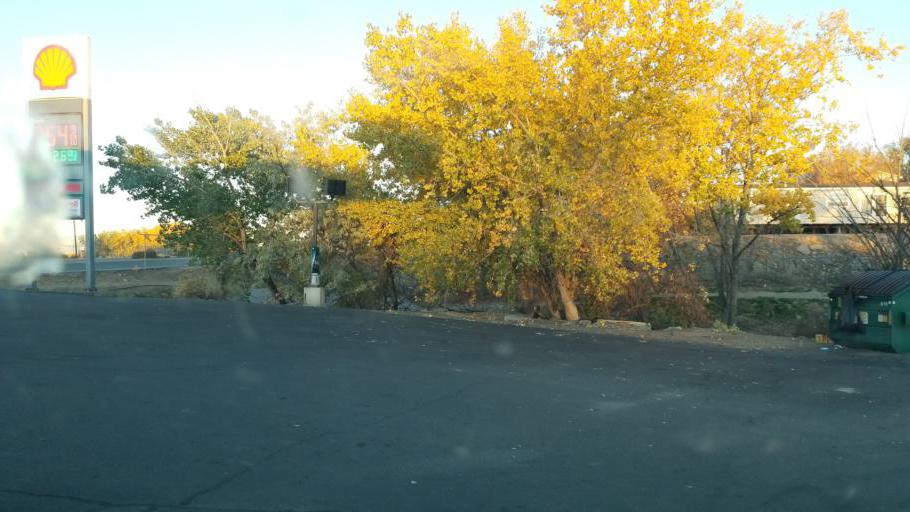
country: US
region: New Mexico
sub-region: San Juan County
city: Farmington
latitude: 36.7301
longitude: -108.2235
